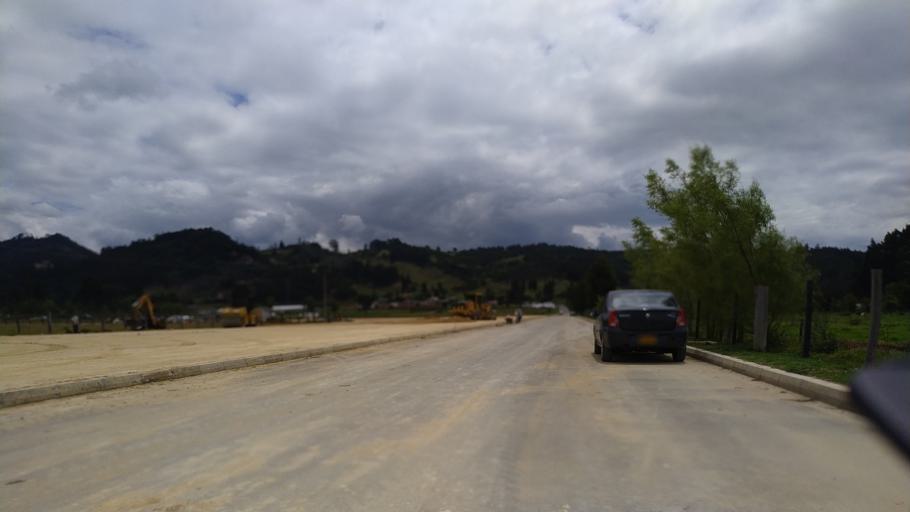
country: CO
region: Boyaca
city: Duitama
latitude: 5.7960
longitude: -73.0687
